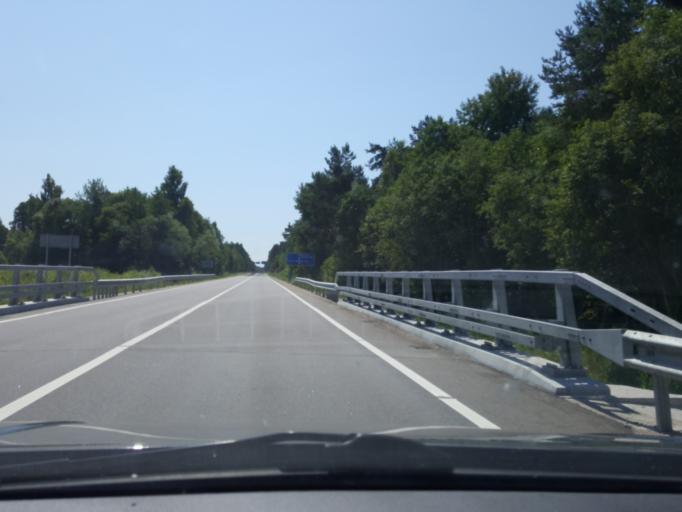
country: LV
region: Rucavas
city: Rucava
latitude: 56.1615
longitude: 21.1461
